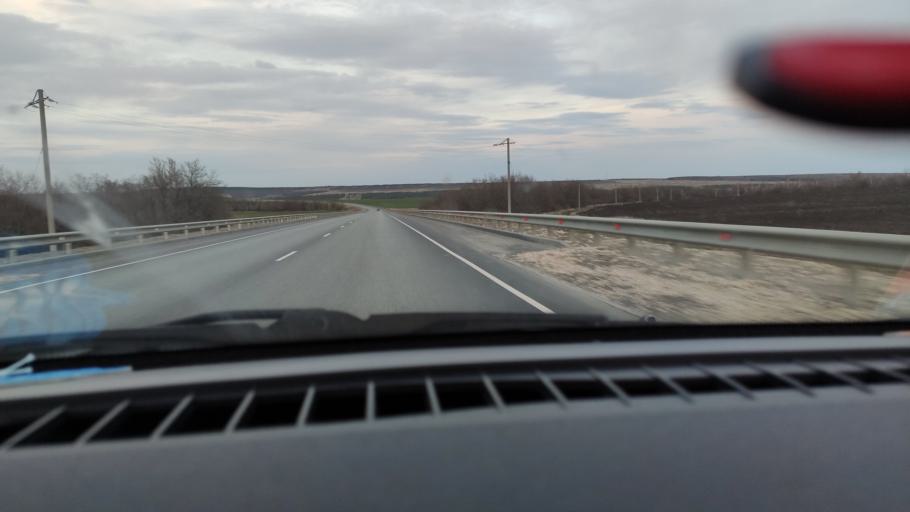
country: RU
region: Saratov
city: Yelshanka
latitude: 51.8310
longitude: 46.4550
